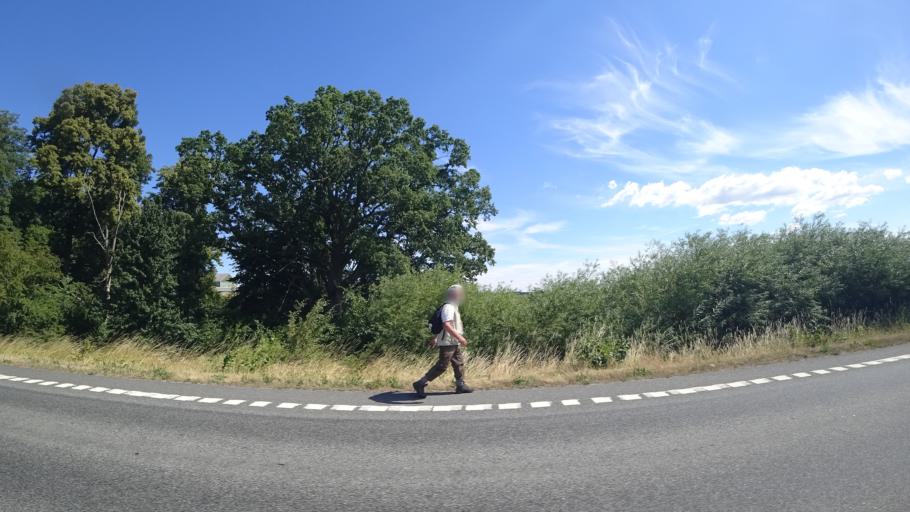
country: SE
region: Skane
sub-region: Kristianstads Kommun
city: Kristianstad
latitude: 56.0440
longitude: 14.0895
